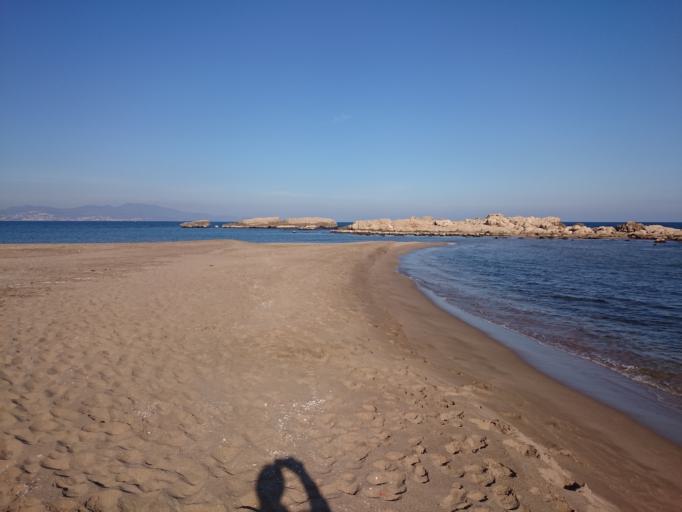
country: ES
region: Catalonia
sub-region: Provincia de Girona
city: l'Escala
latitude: 42.1353
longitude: 3.1220
